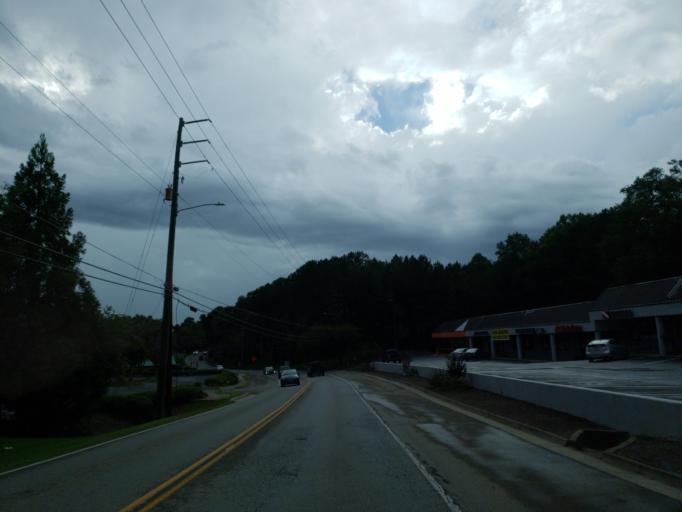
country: US
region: Georgia
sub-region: Cherokee County
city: Woodstock
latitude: 34.1019
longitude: -84.5221
